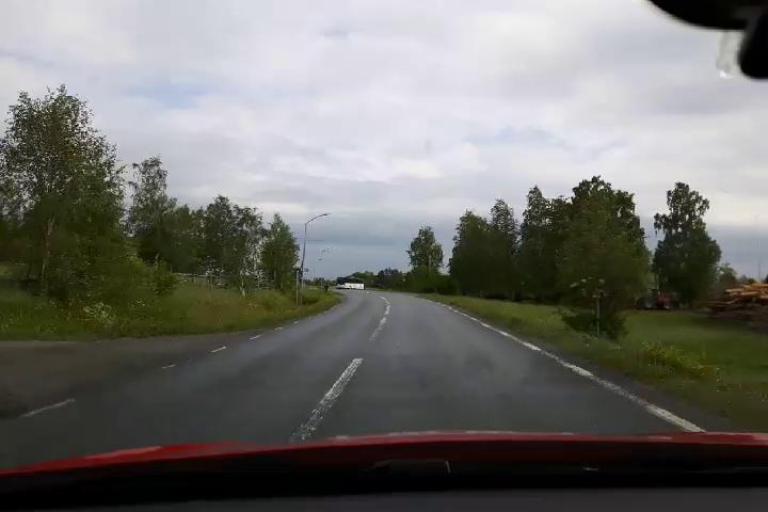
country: SE
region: Jaemtland
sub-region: Bergs Kommun
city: Hoverberg
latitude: 62.9668
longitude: 14.4890
